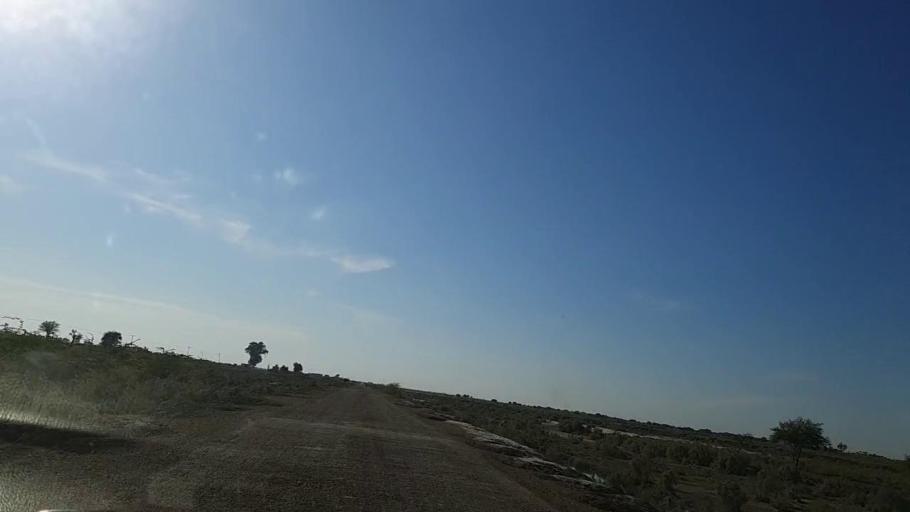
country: PK
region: Sindh
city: Pithoro
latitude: 25.5086
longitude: 69.4510
